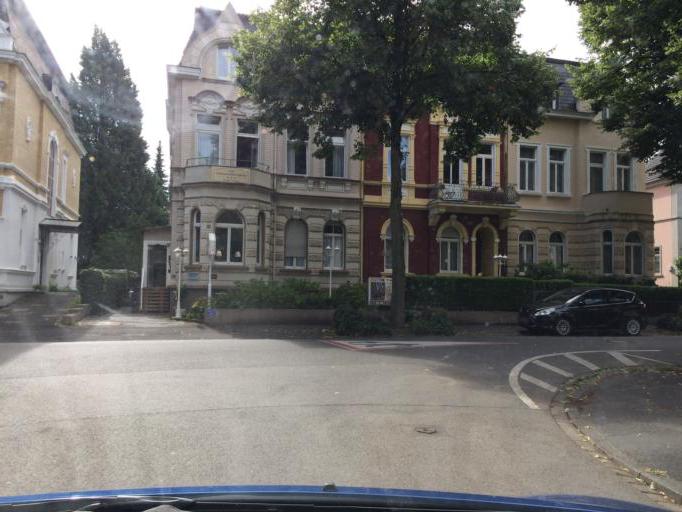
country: DE
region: North Rhine-Westphalia
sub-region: Regierungsbezirk Koln
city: Konigswinter
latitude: 50.6905
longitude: 7.1557
